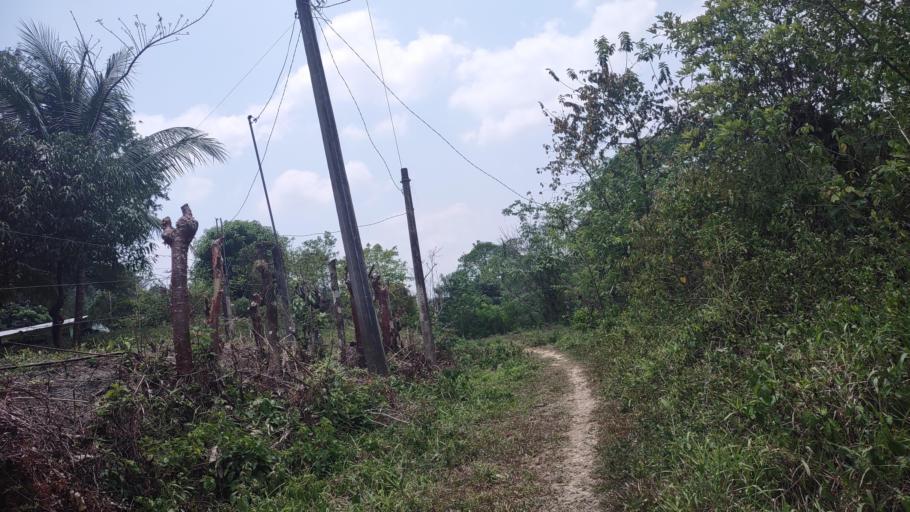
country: MX
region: Tabasco
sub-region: Huimanguillo
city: Francisco Rueda
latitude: 17.6484
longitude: -93.9069
